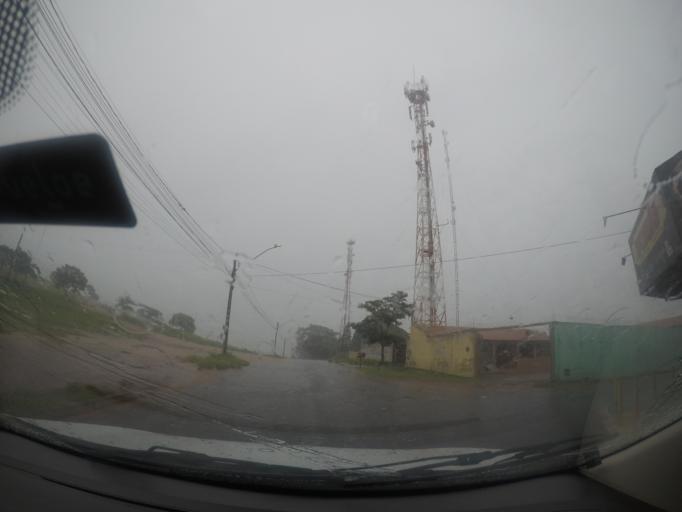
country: BR
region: Goias
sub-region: Goiania
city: Goiania
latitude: -16.6047
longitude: -49.3296
